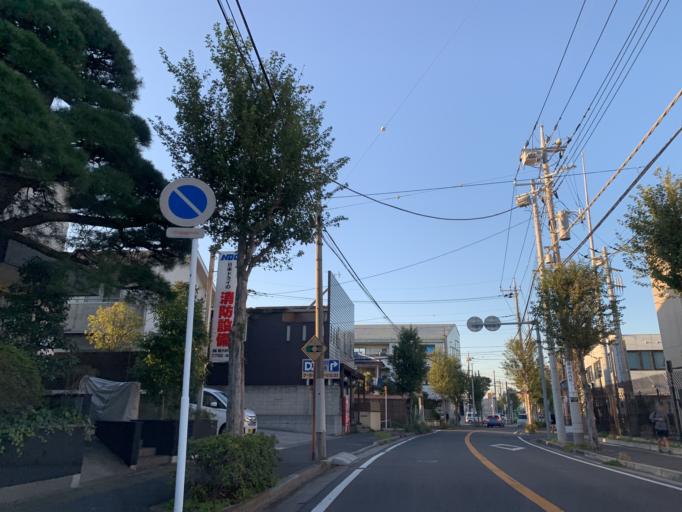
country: JP
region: Chiba
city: Nagareyama
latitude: 35.8978
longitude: 139.9127
